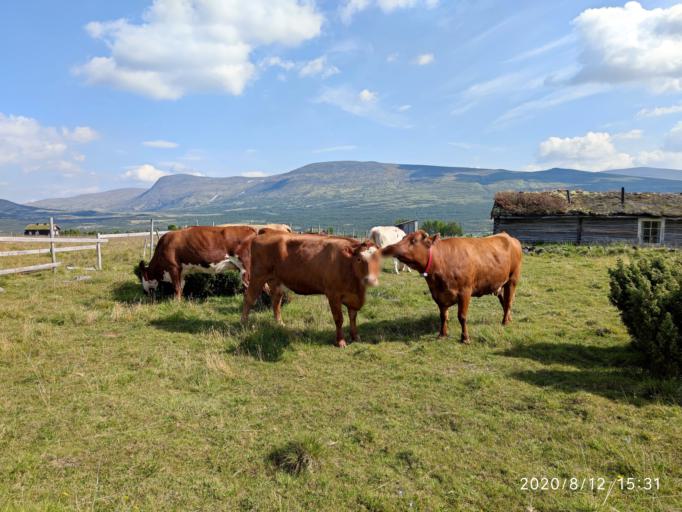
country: NO
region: Oppland
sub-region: Dovre
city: Dovre
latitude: 62.1562
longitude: 9.2979
